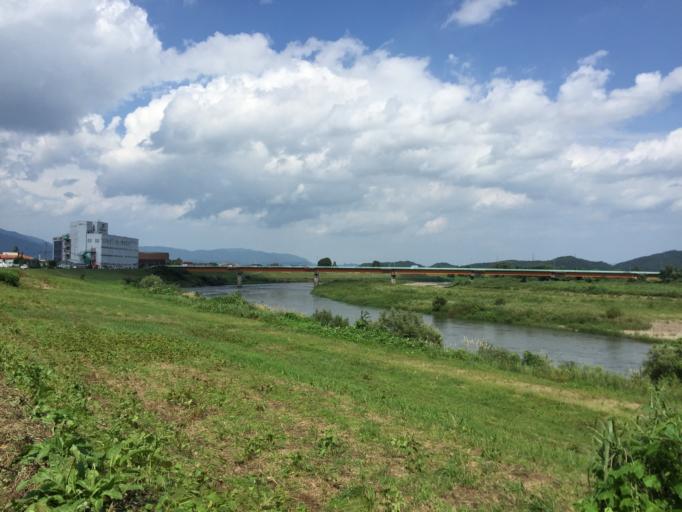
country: JP
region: Fukushima
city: Fukushima-shi
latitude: 37.7869
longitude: 140.4882
